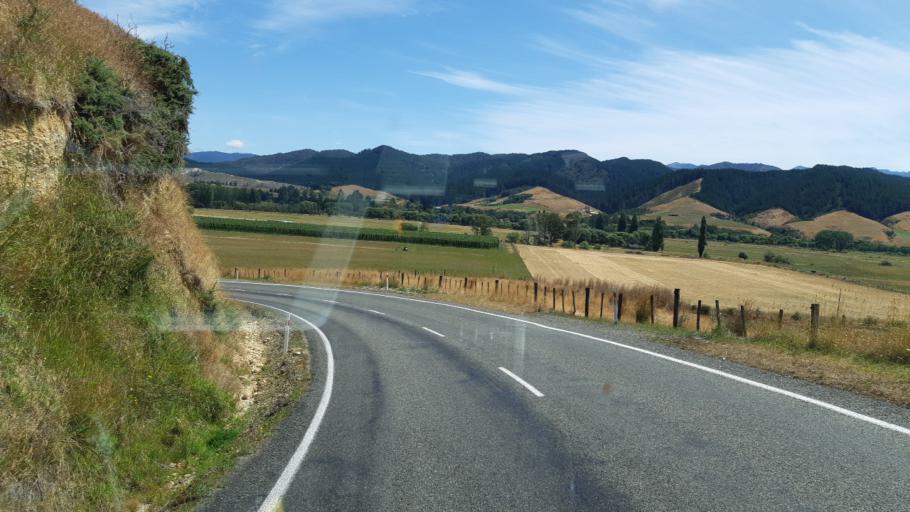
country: NZ
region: Tasman
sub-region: Tasman District
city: Wakefield
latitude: -41.3433
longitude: 172.8092
